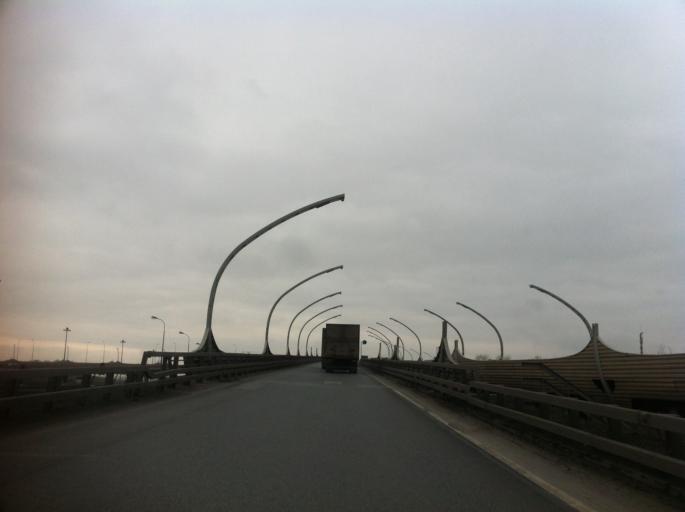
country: RU
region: St.-Petersburg
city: Dachnoye
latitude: 59.8357
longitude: 30.2745
